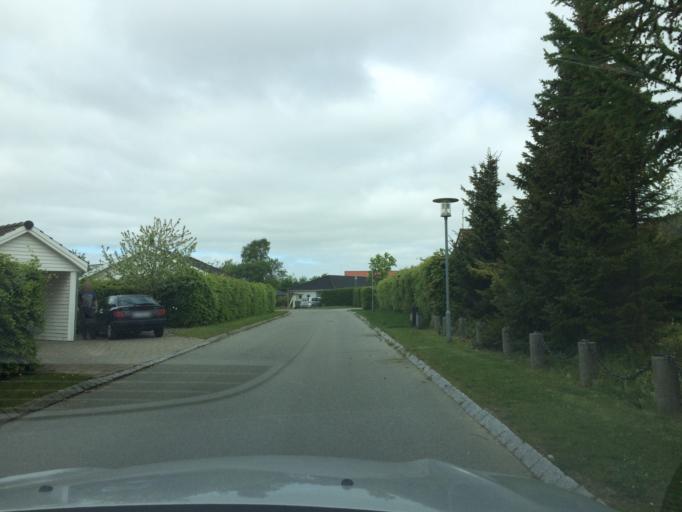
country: DK
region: Central Jutland
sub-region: Arhus Kommune
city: Logten
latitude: 56.2365
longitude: 10.3095
